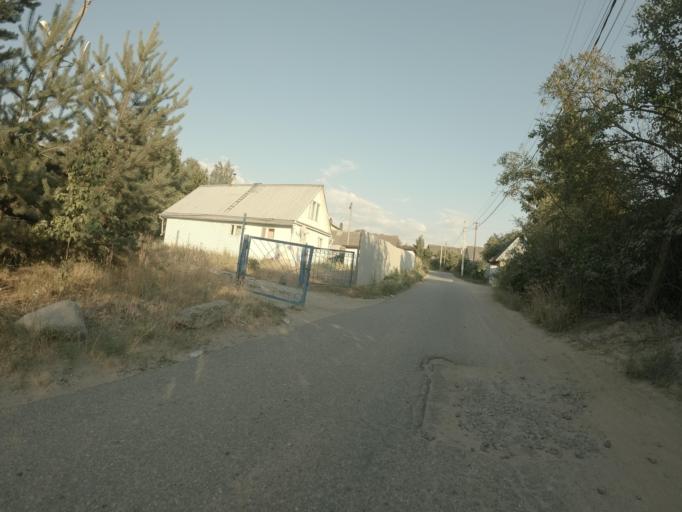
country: RU
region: Leningrad
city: Koltushi
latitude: 59.8961
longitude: 30.6864
